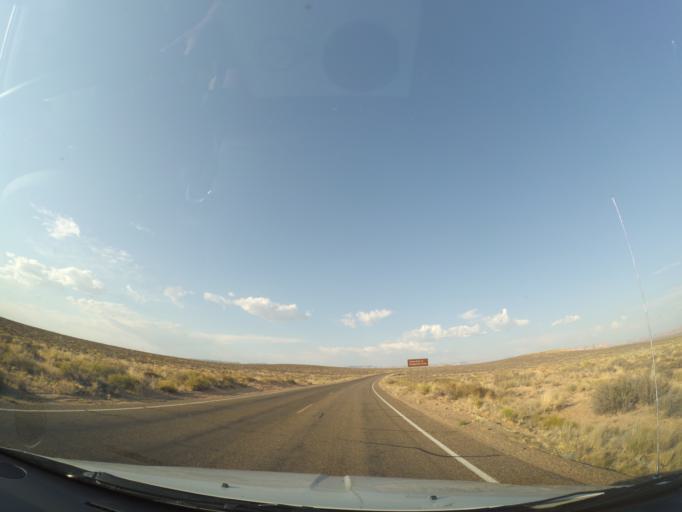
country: US
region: Arizona
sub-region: Coconino County
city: Page
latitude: 36.9824
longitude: -111.5260
